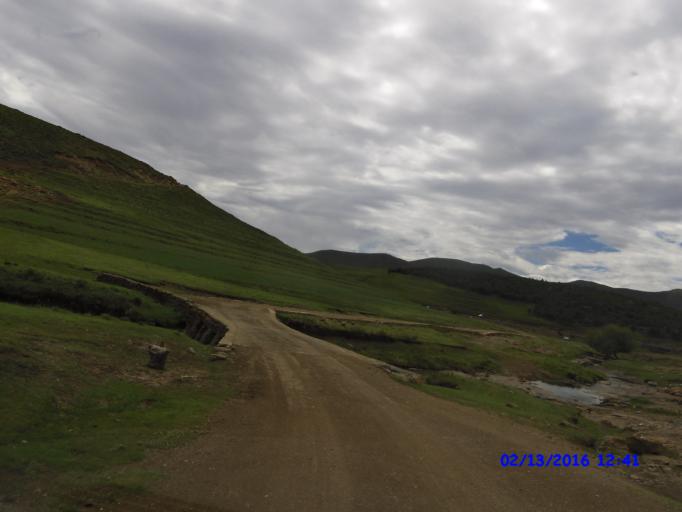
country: LS
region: Maseru
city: Nako
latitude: -29.8301
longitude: 28.0353
